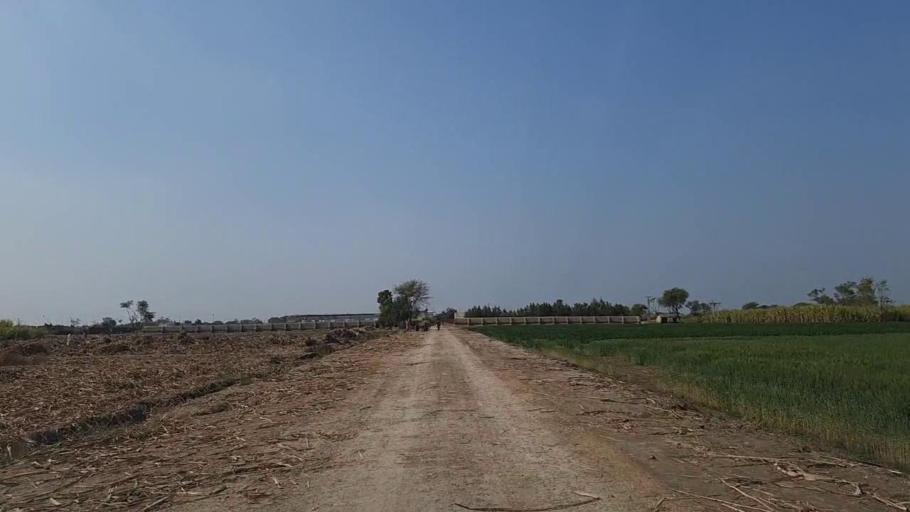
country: PK
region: Sindh
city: Nawabshah
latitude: 26.2871
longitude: 68.4873
